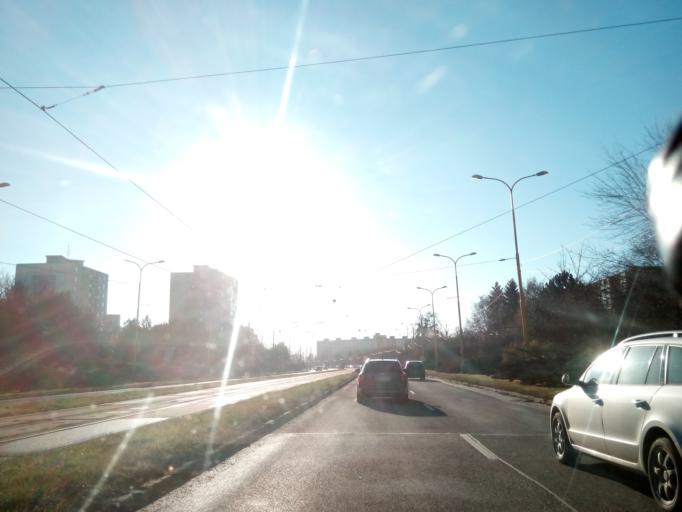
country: SK
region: Kosicky
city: Kosice
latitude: 48.7124
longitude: 21.2358
